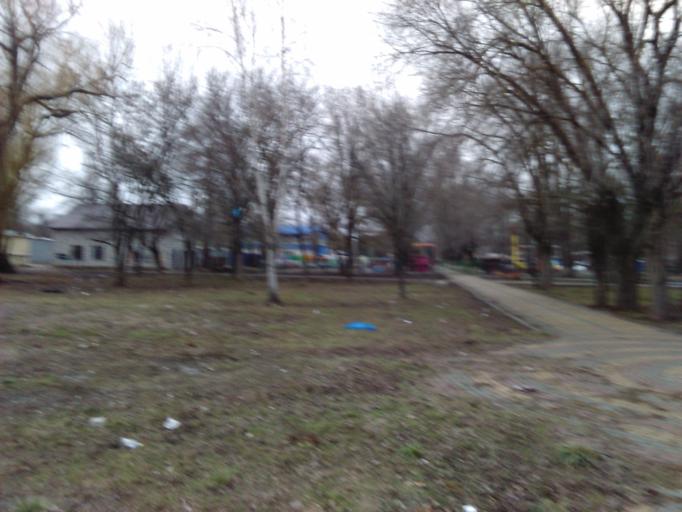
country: RU
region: Rostov
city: Bataysk
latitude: 47.1351
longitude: 39.7424
